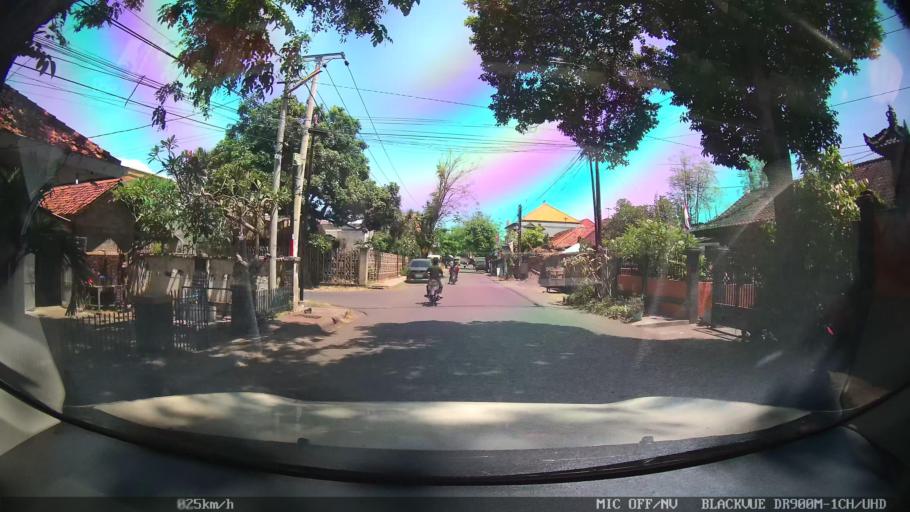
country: ID
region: Bali
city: Banjar Kampunganyar
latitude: -8.1073
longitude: 115.0849
